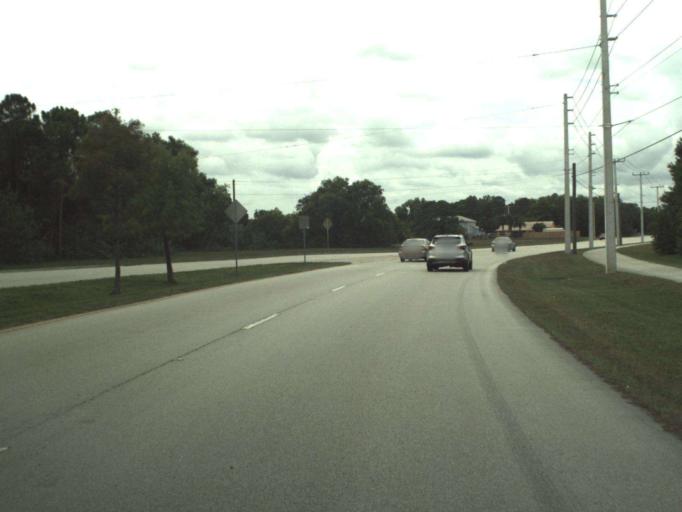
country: US
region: Florida
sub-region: Saint Lucie County
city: River Park
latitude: 27.3402
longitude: -80.3507
